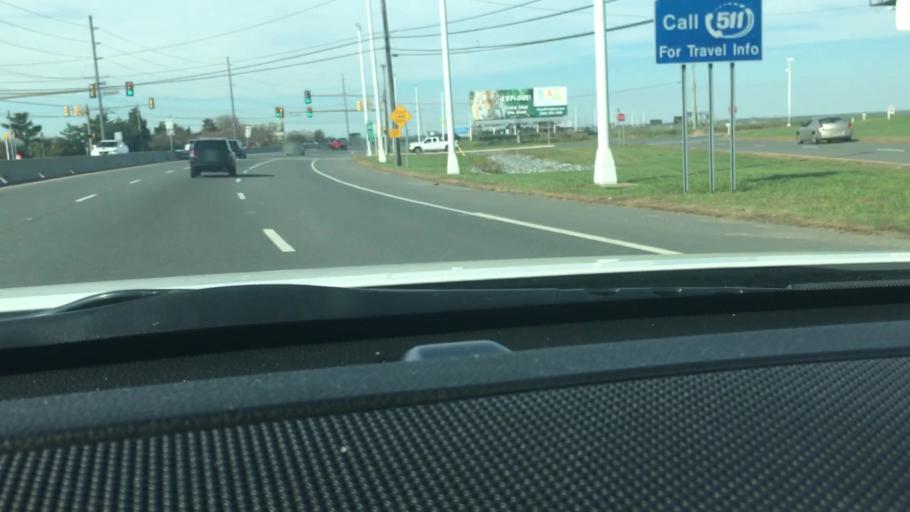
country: US
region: New Jersey
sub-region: Atlantic County
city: Atlantic City
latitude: 39.3788
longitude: -74.4564
